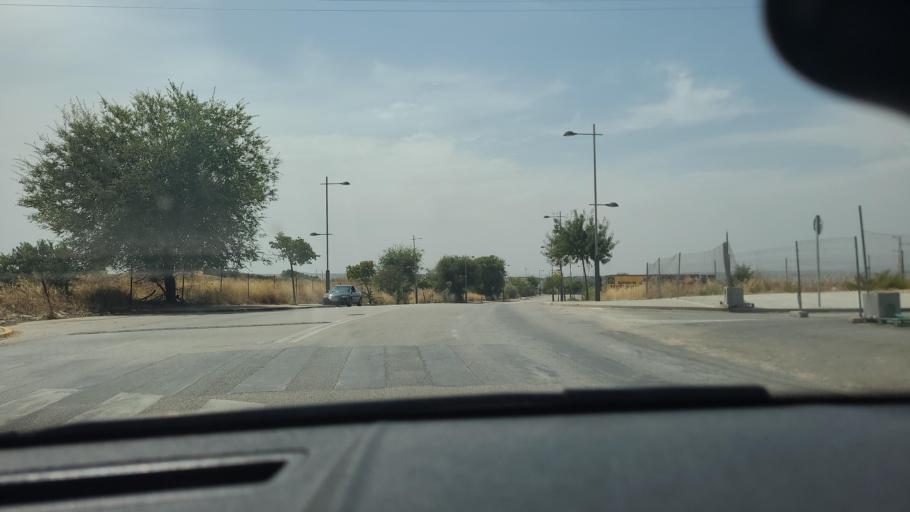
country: ES
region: Andalusia
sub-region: Provincia de Jaen
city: Linares
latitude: 38.0870
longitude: -3.6315
